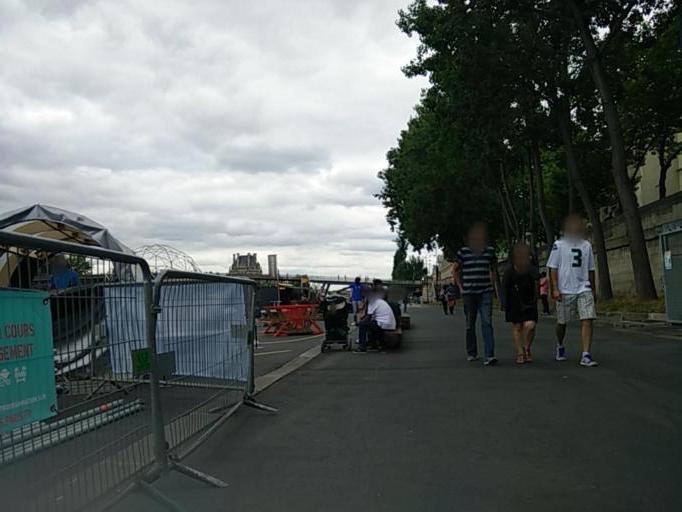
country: FR
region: Ile-de-France
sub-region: Paris
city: Paris
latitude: 48.8618
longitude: 2.3225
